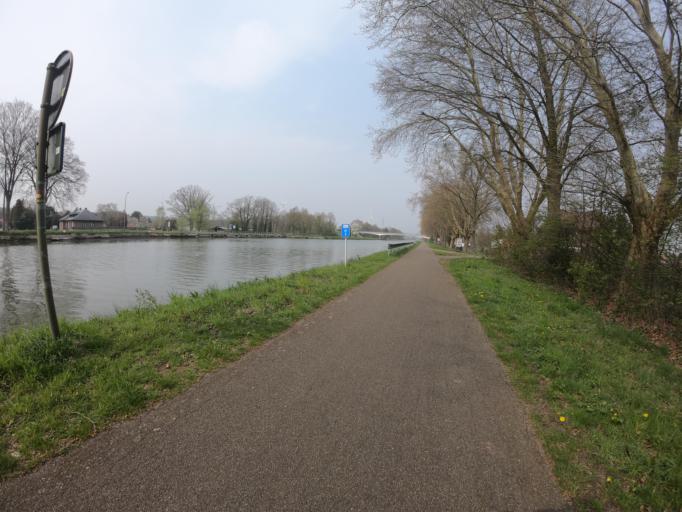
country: BE
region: Flanders
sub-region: Provincie Limburg
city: Maasmechelen
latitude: 51.0359
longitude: 5.7056
